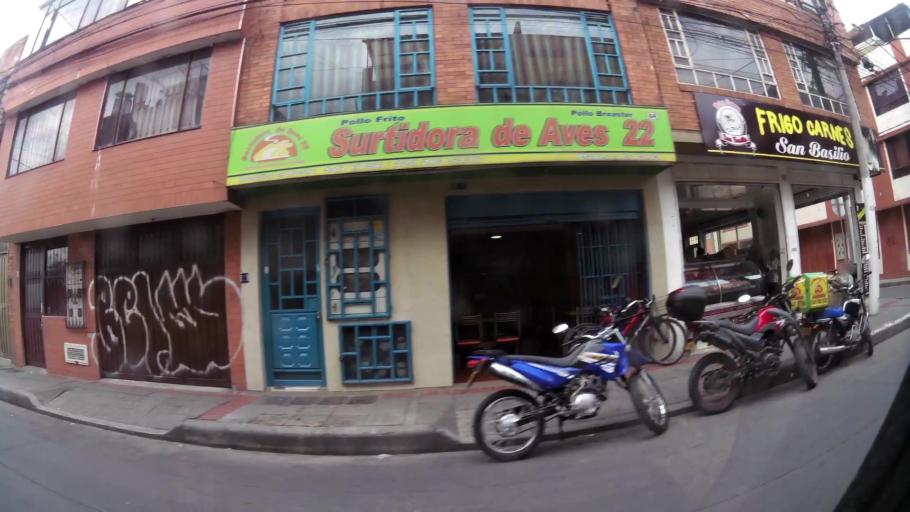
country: CO
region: Cundinamarca
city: Funza
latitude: 4.7025
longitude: -74.1232
